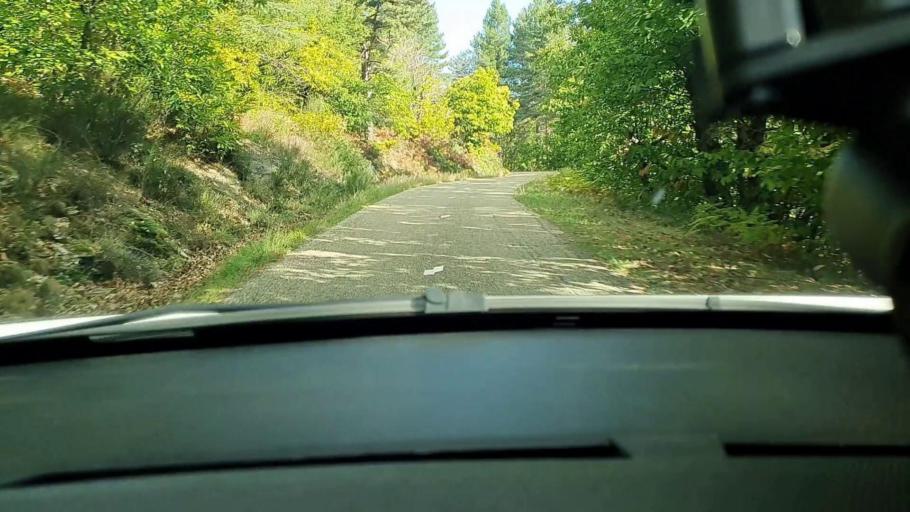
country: FR
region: Languedoc-Roussillon
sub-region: Departement du Gard
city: Besseges
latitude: 44.3749
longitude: 3.9912
